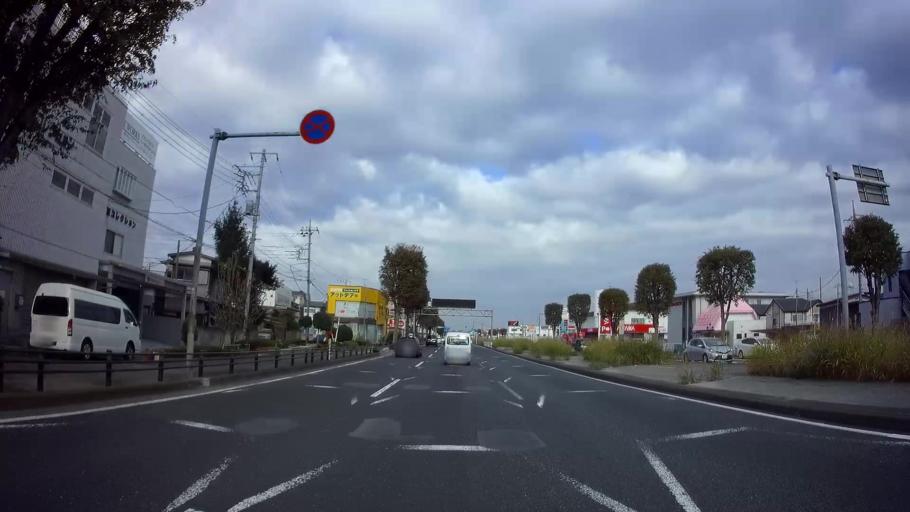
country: JP
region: Saitama
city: Yono
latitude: 35.8956
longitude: 139.6060
